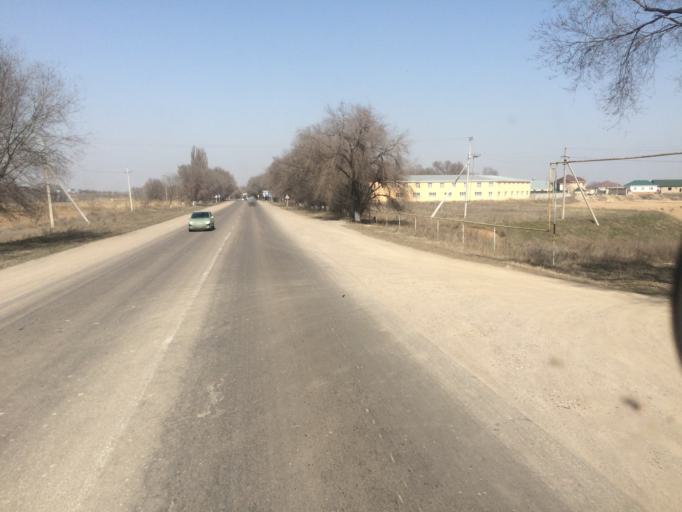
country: KZ
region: Almaty Oblysy
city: Burunday
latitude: 43.2974
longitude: 76.6729
